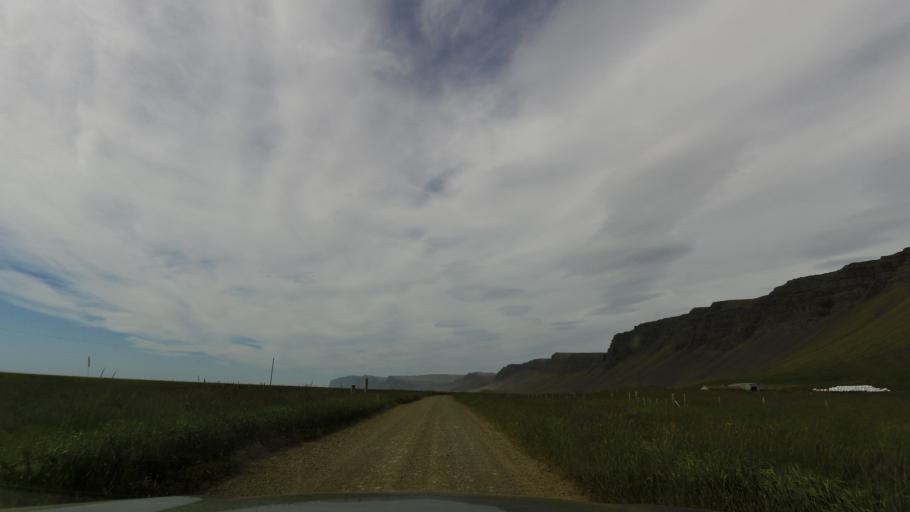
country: IS
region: West
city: Olafsvik
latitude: 65.4847
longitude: -24.0546
